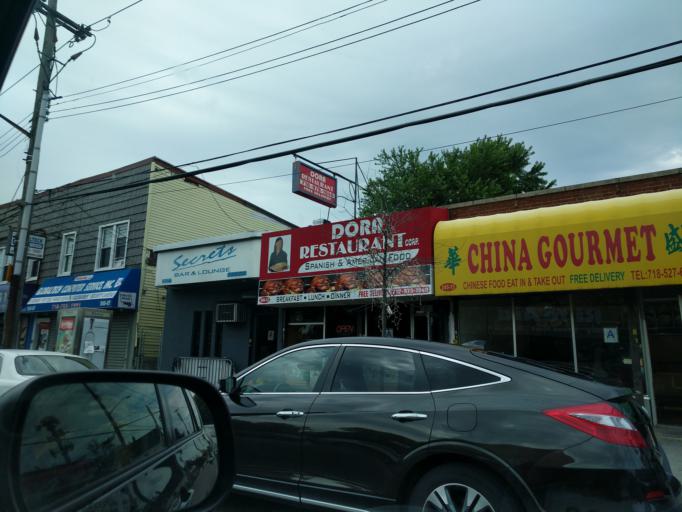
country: US
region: New York
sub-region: Nassau County
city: South Valley Stream
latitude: 40.6647
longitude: -73.7347
